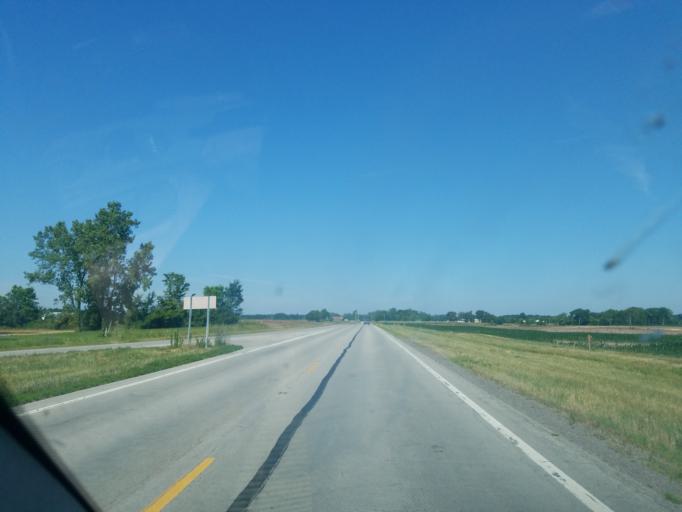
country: US
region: Ohio
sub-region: Logan County
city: Russells Point
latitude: 40.4650
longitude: -83.8143
